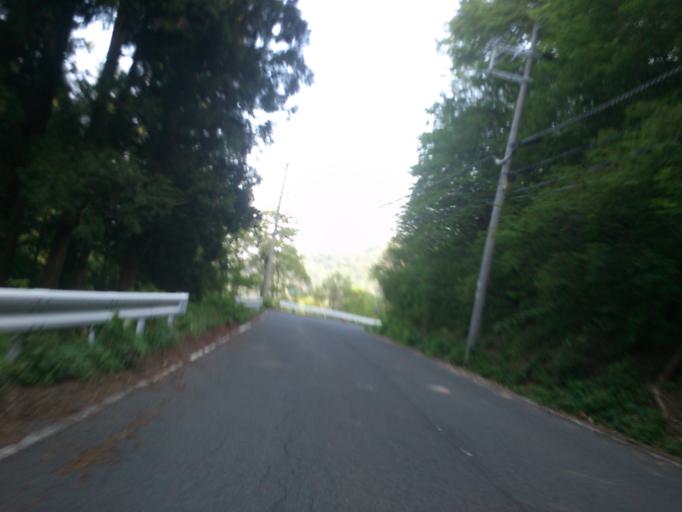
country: JP
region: Kyoto
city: Miyazu
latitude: 35.7127
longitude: 135.1932
